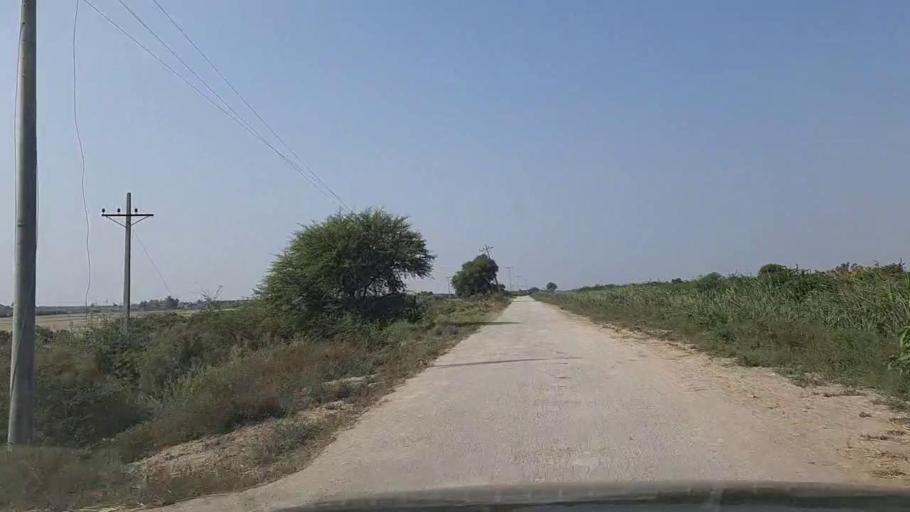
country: PK
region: Sindh
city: Gharo
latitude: 24.7374
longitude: 67.7523
